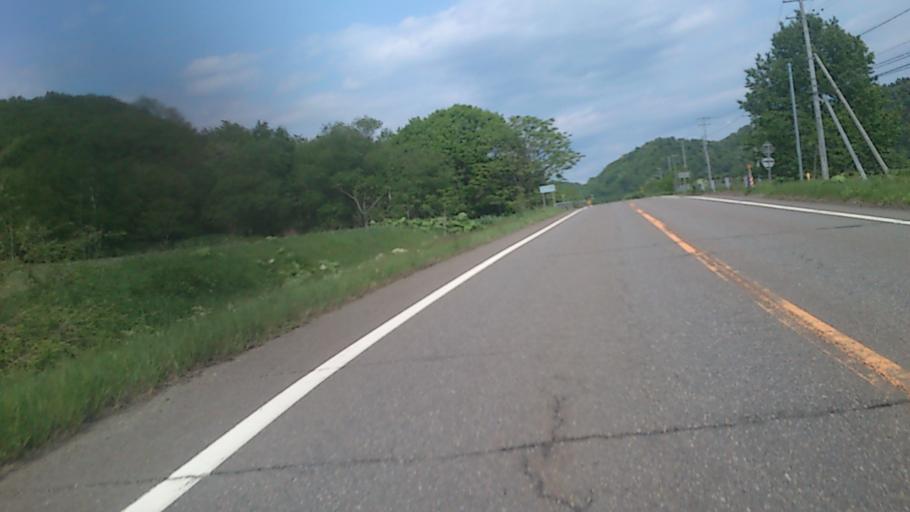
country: JP
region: Hokkaido
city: Kitami
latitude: 43.3428
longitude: 143.7638
